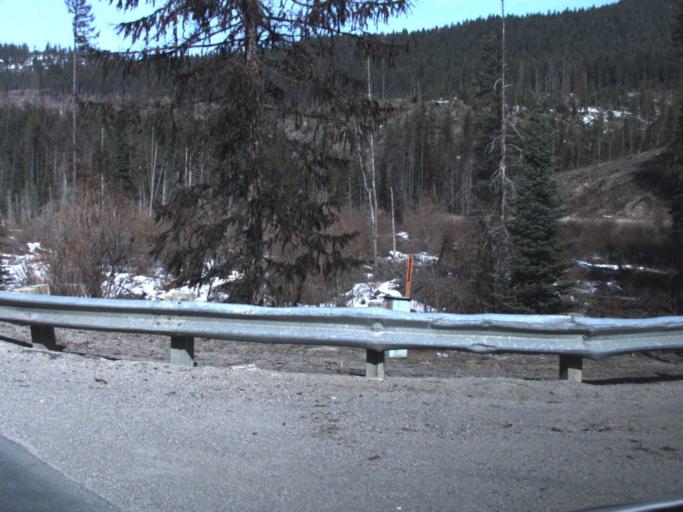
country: US
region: Washington
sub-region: Stevens County
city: Chewelah
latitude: 48.5398
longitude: -117.5940
